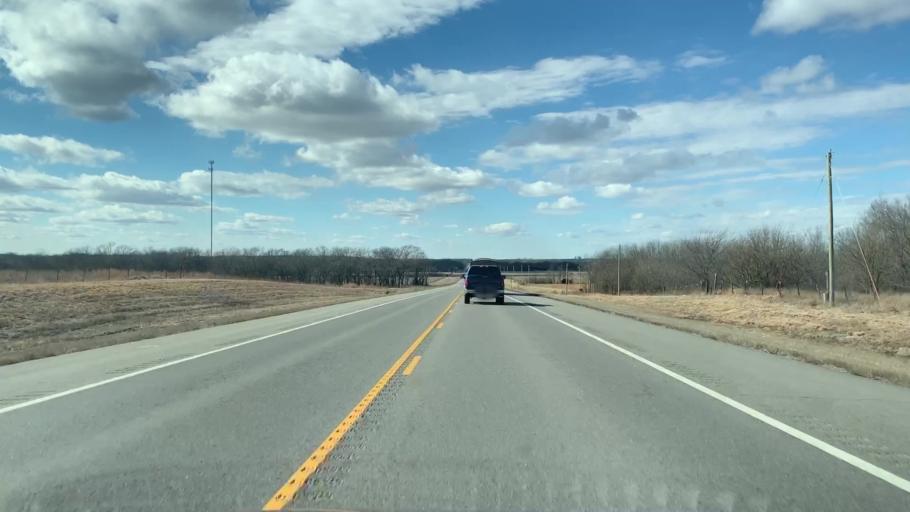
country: US
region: Kansas
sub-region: Cherokee County
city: Columbus
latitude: 37.3400
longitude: -94.9099
